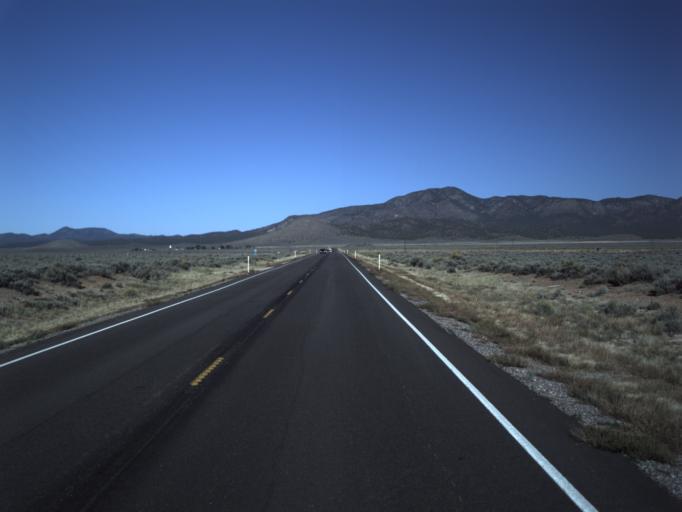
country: US
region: Utah
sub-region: Washington County
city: Enterprise
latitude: 37.7915
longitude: -113.8905
